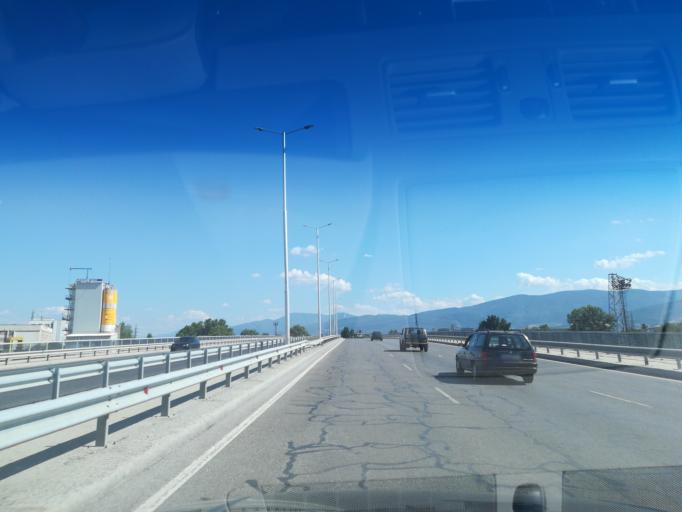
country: BG
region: Plovdiv
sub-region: Obshtina Plovdiv
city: Plovdiv
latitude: 42.1187
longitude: 24.7760
